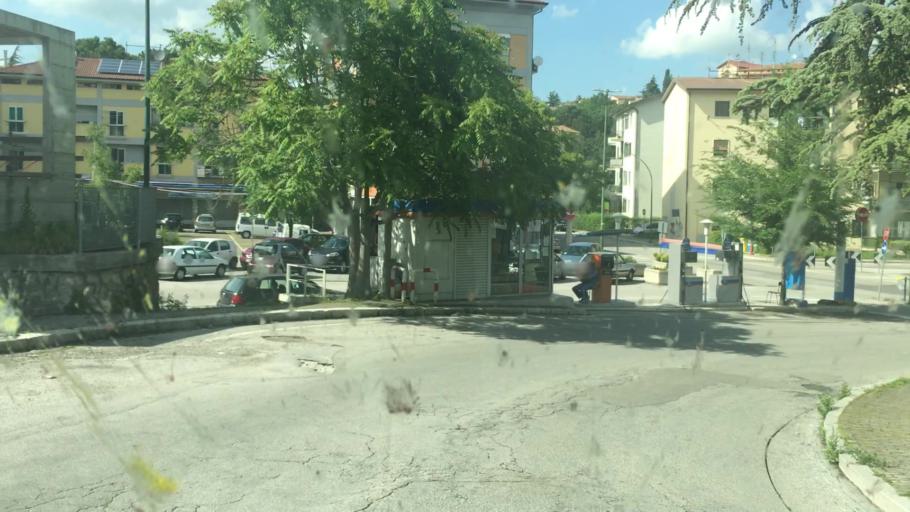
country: IT
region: Basilicate
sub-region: Provincia di Potenza
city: Potenza
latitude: 40.6441
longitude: 15.7982
